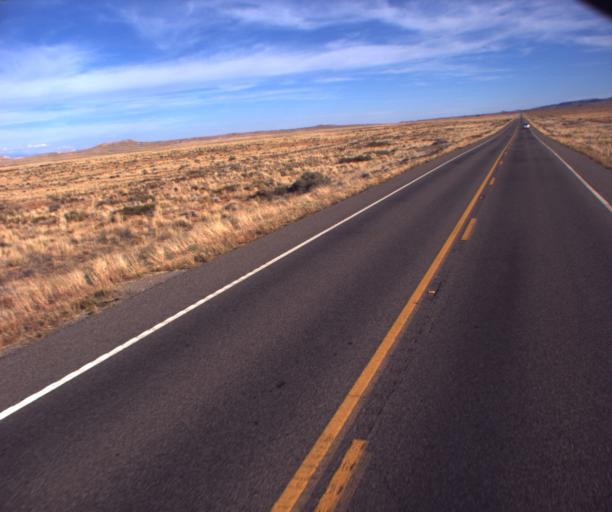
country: US
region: Arizona
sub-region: Apache County
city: Lukachukai
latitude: 36.9497
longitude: -109.2805
